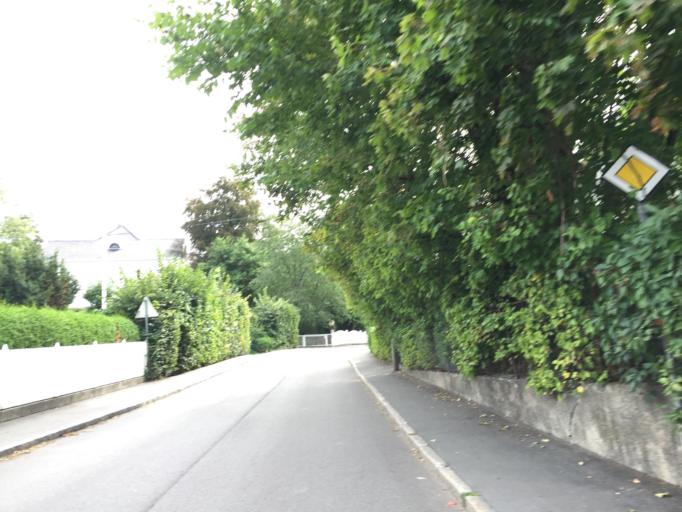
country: NO
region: Oslo
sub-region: Oslo
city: Sjolyststranda
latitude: 59.9043
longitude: 10.6865
